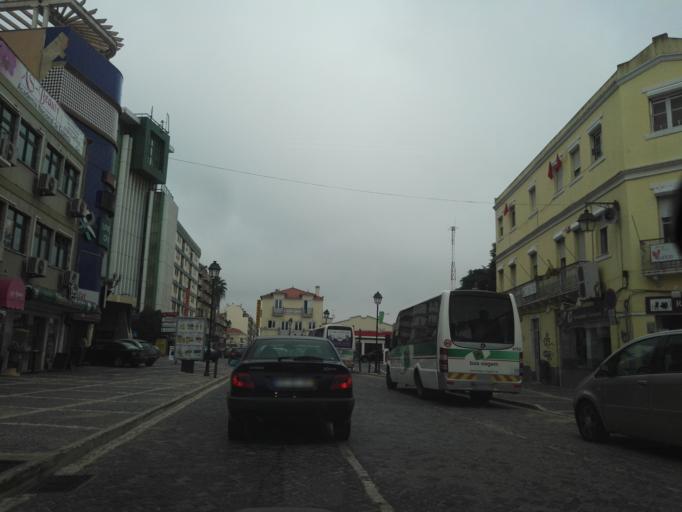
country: PT
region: Lisbon
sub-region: Vila Franca de Xira
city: Vila Franca de Xira
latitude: 38.9549
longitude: -8.9869
